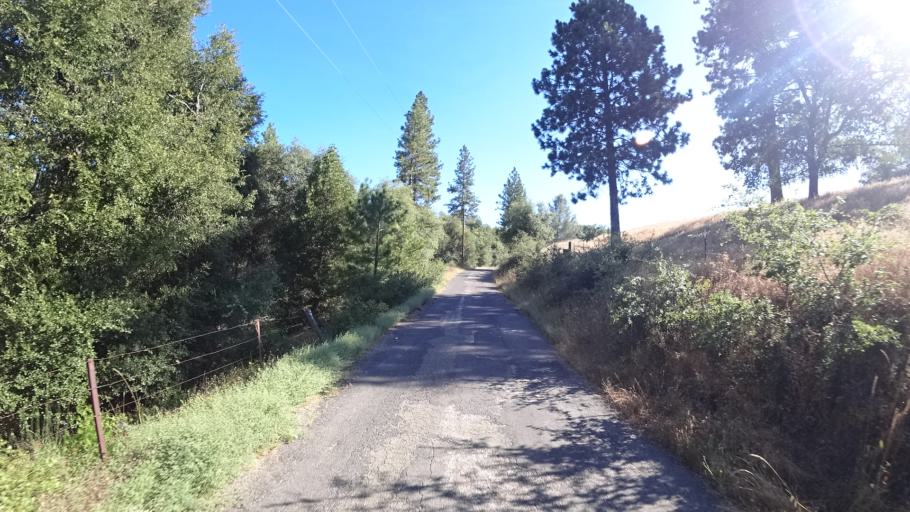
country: US
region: California
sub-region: Amador County
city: Pioneer
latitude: 38.3949
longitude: -120.5822
